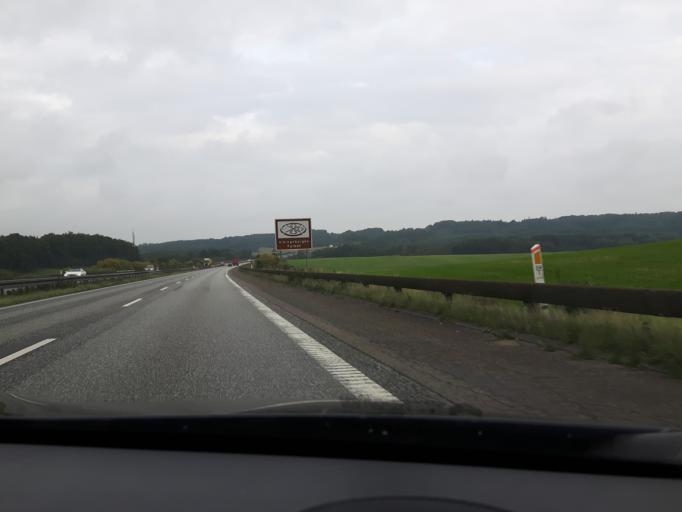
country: DK
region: North Denmark
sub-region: Mariagerfjord Kommune
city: Hobro
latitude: 56.6084
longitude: 9.7422
